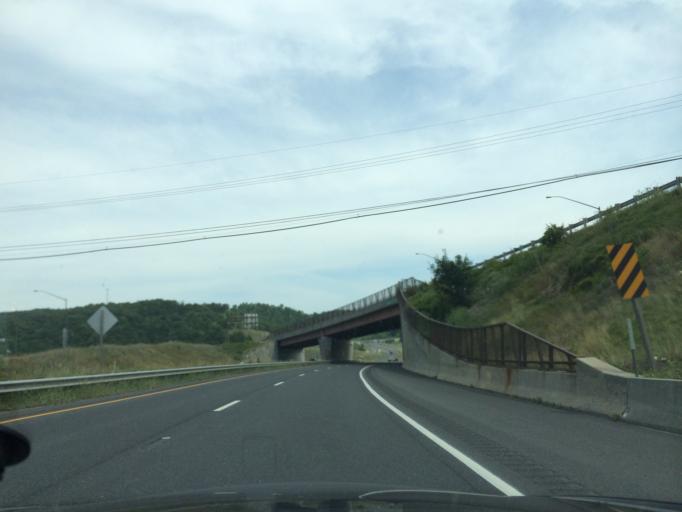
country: US
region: Maryland
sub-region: Allegany County
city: Cumberland
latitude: 39.6733
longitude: -78.7162
